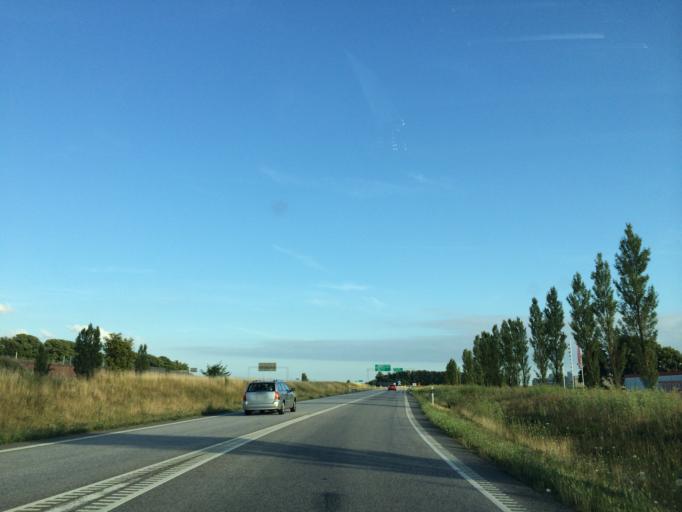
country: SE
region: Skane
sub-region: Malmo
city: Tygelsjo
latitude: 55.5528
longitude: 12.9992
